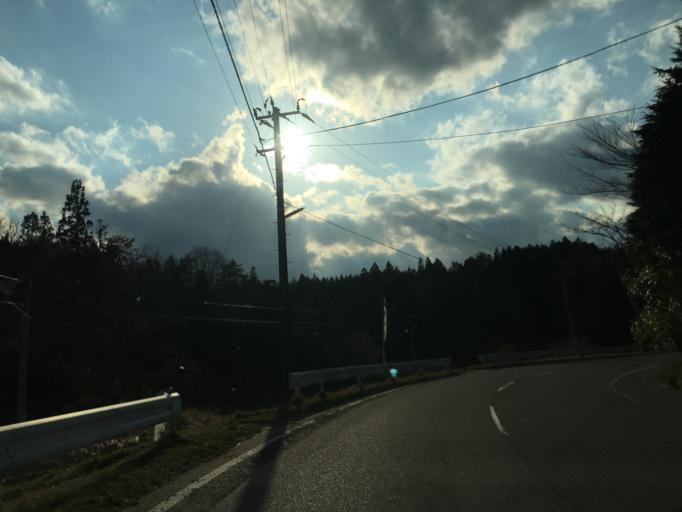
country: JP
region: Fukushima
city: Ishikawa
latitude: 37.1757
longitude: 140.5985
